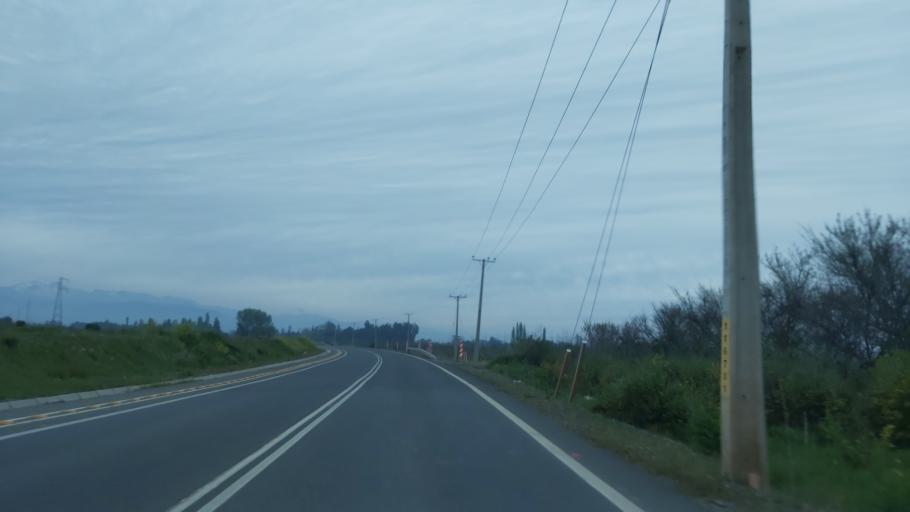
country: CL
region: Maule
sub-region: Provincia de Linares
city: Colbun
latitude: -35.7031
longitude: -71.4858
